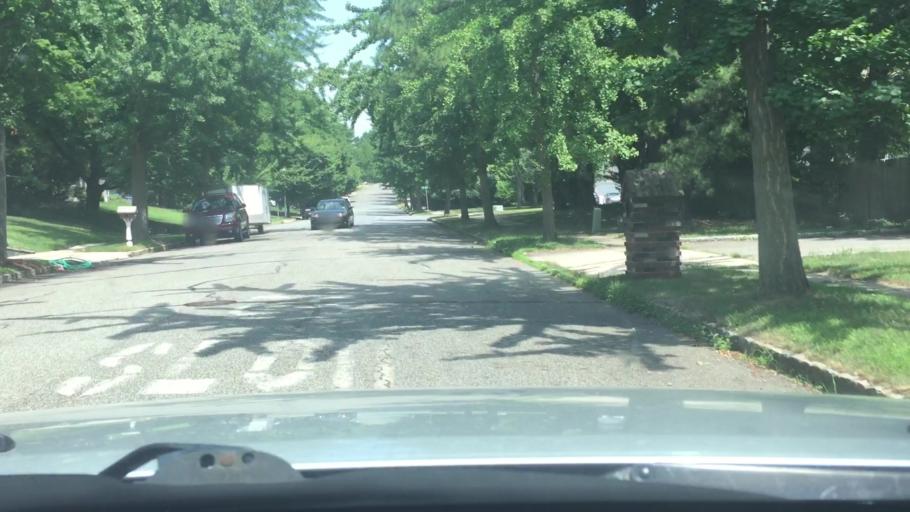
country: US
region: New Jersey
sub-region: Middlesex County
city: Spotswood
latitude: 40.4054
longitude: -74.4040
